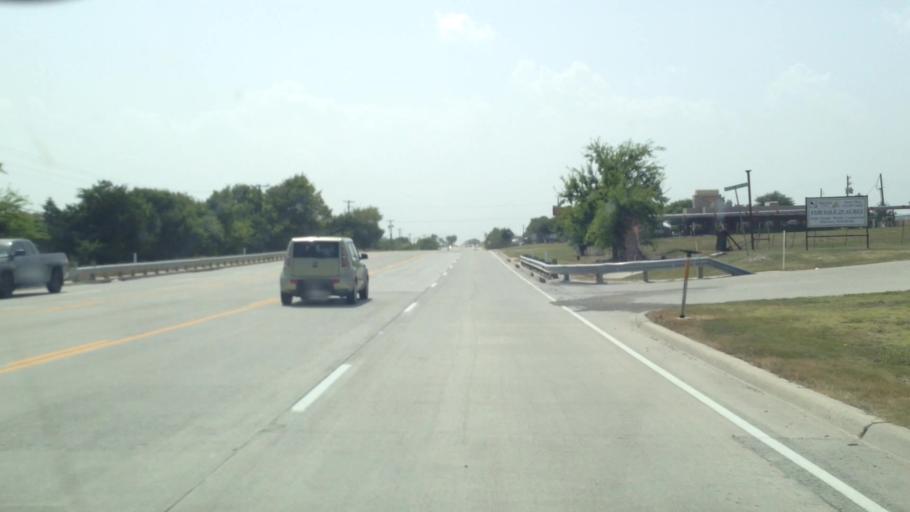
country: US
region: Texas
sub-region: Collin County
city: Farmersville
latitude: 33.1572
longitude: -96.3697
